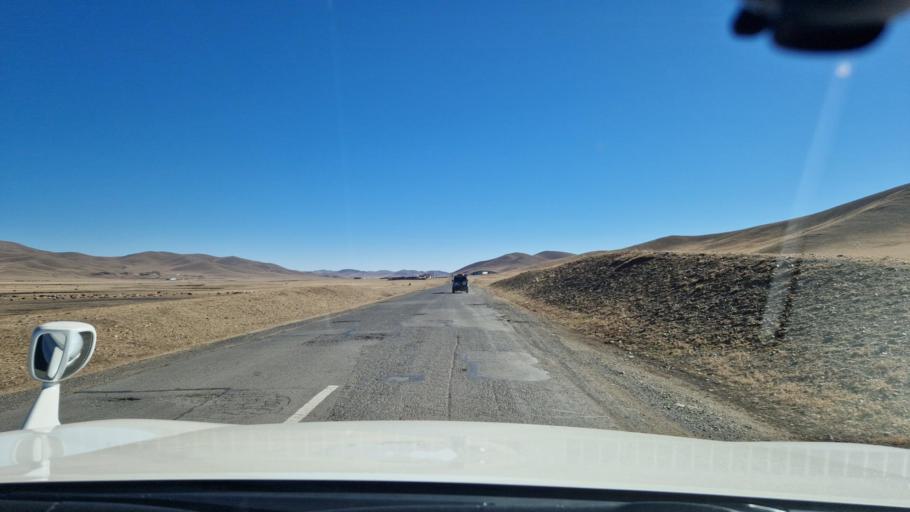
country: MN
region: Hentiy
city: Modot
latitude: 47.7312
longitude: 109.0113
